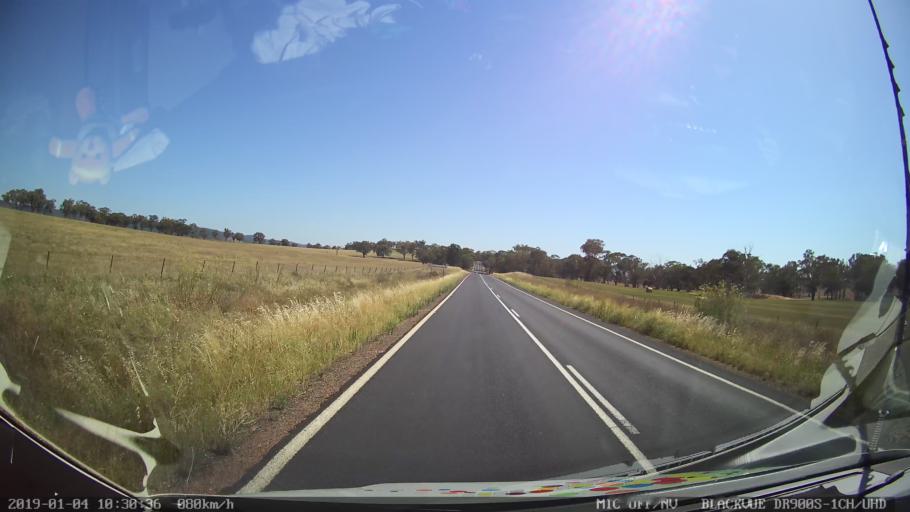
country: AU
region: New South Wales
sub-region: Cabonne
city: Canowindra
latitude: -33.3439
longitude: 148.6287
